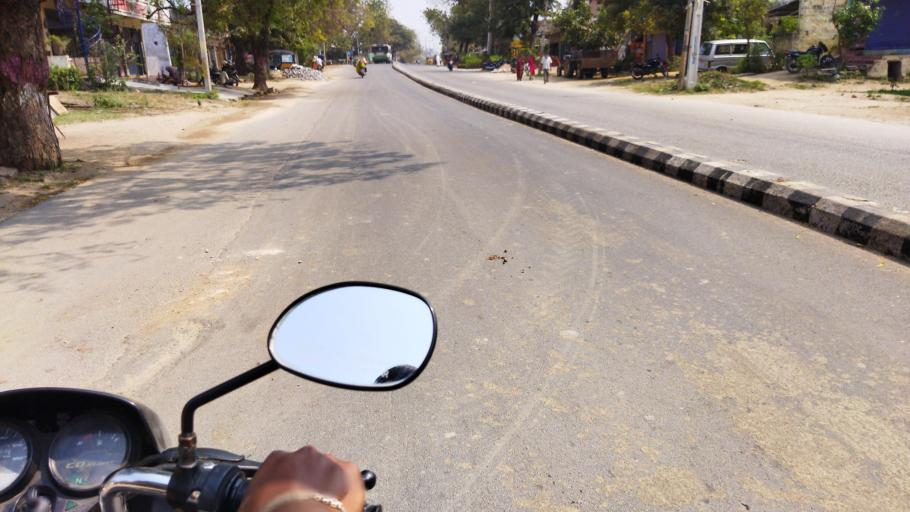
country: IN
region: Telangana
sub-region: Nalgonda
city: Nalgonda
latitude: 17.1665
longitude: 79.4203
